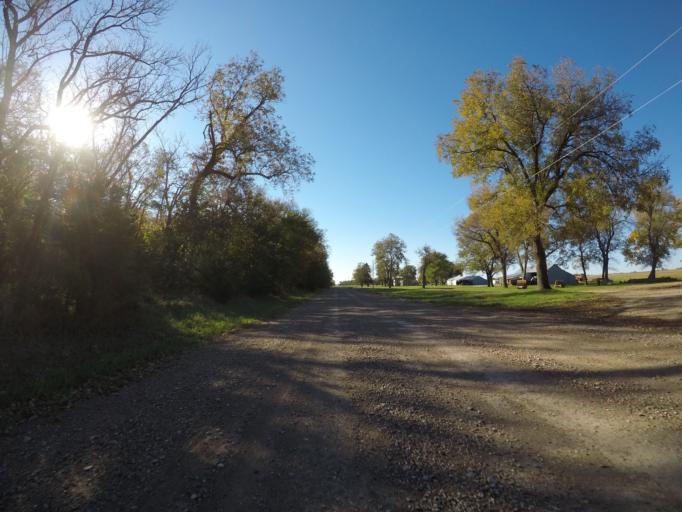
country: US
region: Kansas
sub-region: Morris County
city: Council Grove
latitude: 38.8477
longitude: -96.4829
